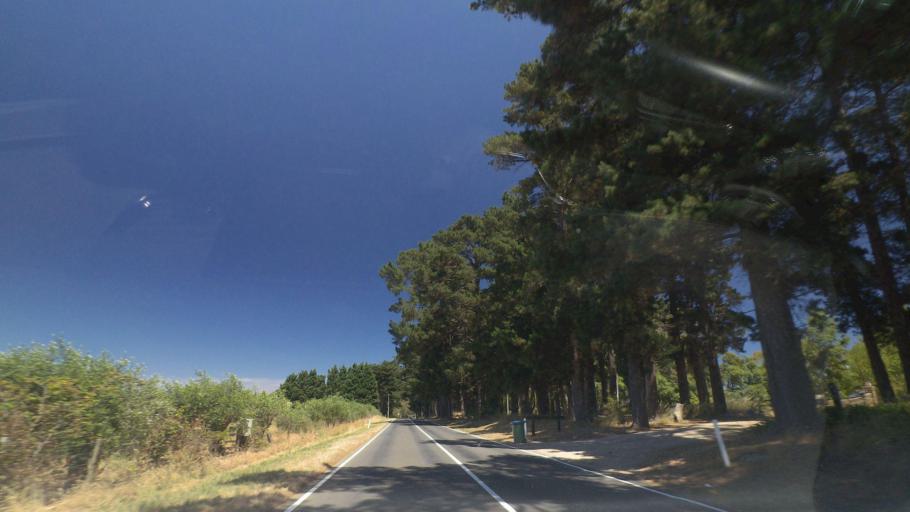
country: AU
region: Victoria
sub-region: Mornington Peninsula
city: Dromana
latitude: -38.3783
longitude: 144.9764
